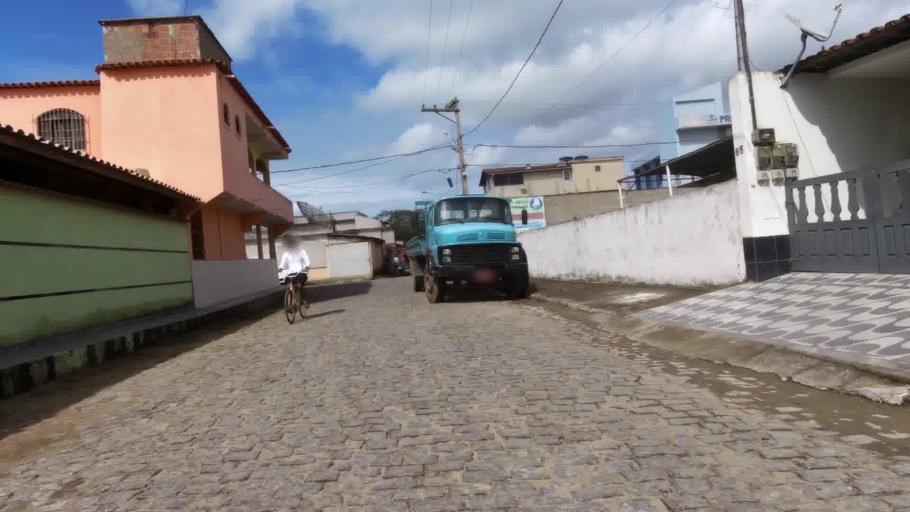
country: BR
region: Espirito Santo
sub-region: Marataizes
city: Marataizes
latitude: -21.0334
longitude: -40.8186
